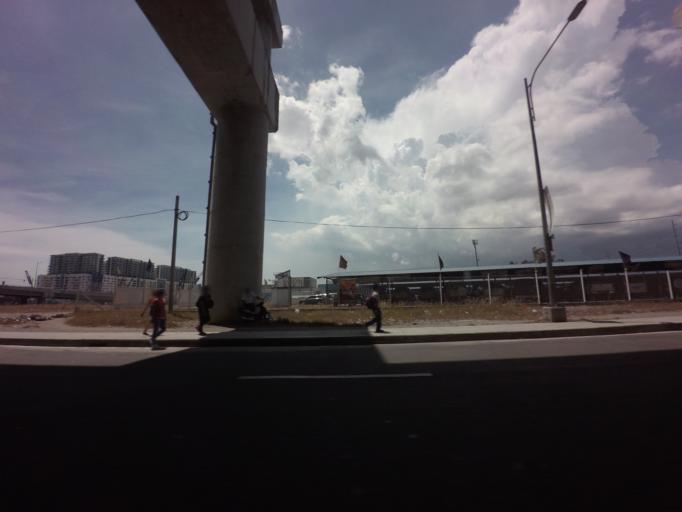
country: PH
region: Metro Manila
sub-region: Makati City
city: Makati City
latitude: 14.5177
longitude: 120.9919
